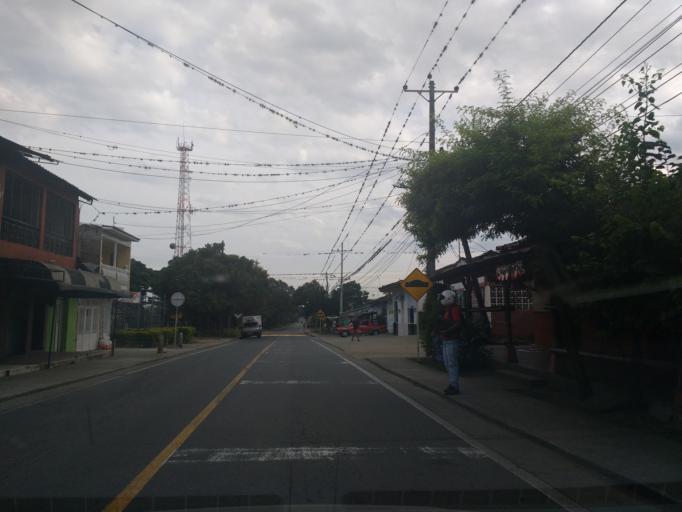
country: CO
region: Cauca
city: Miranda
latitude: 3.2839
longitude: -76.2243
